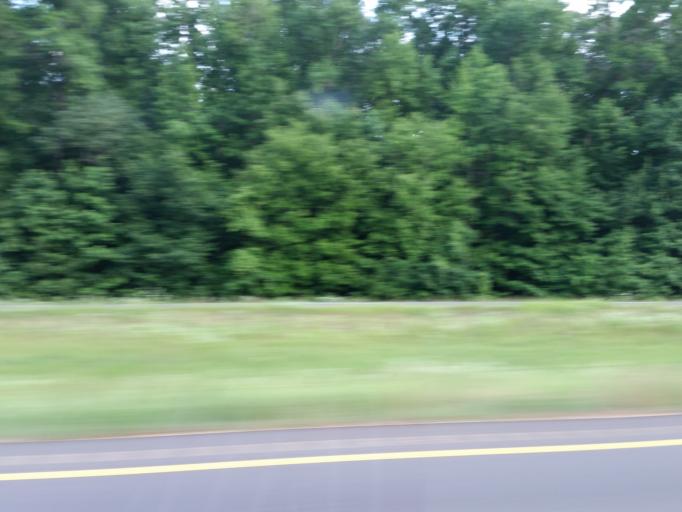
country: US
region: Tennessee
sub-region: Henry County
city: Paris
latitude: 36.3496
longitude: -88.2310
